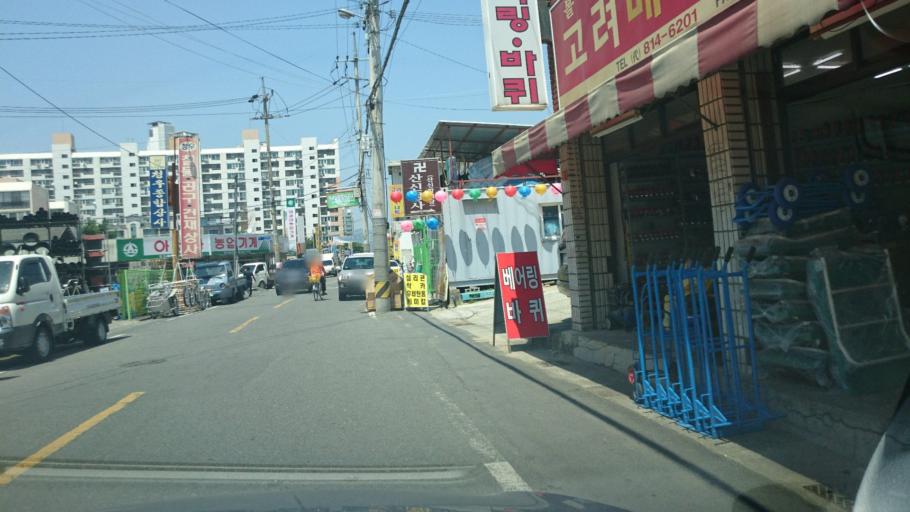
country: KR
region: Gyeongsangbuk-do
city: Gyeongsan-si
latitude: 35.8280
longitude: 128.7383
